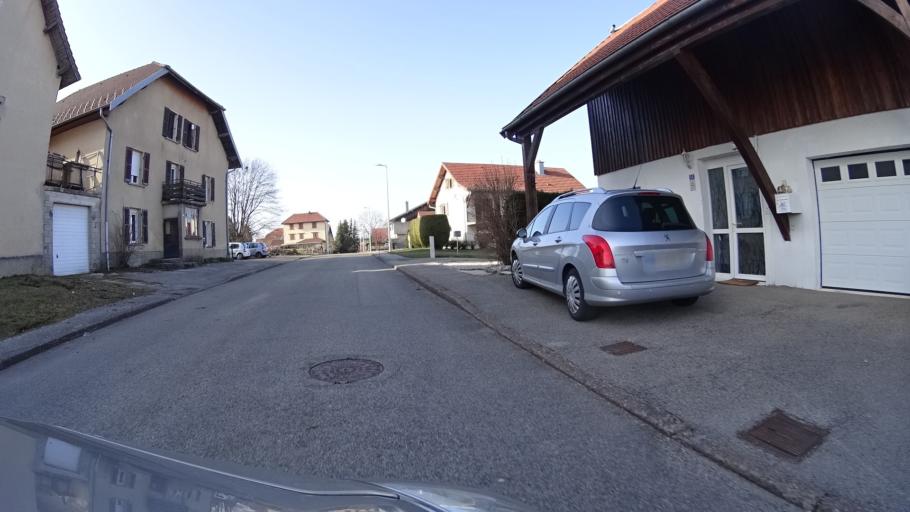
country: FR
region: Franche-Comte
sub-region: Departement du Doubs
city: Frasne
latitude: 46.8912
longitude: 6.2208
